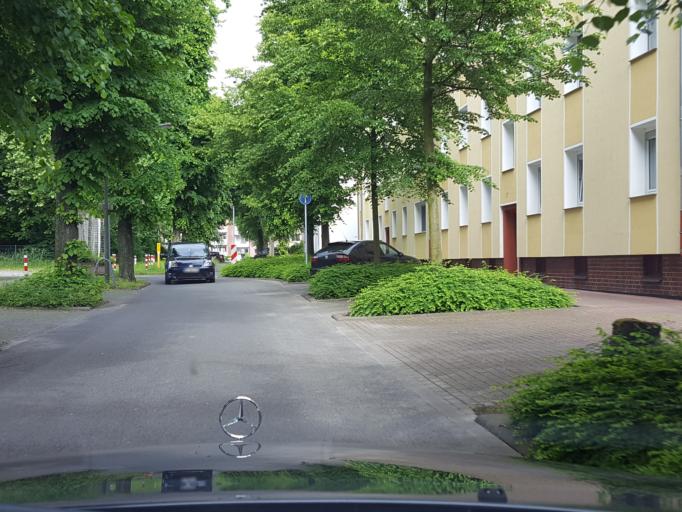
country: DE
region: North Rhine-Westphalia
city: Oer-Erkenschwick
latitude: 51.6412
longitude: 7.2745
